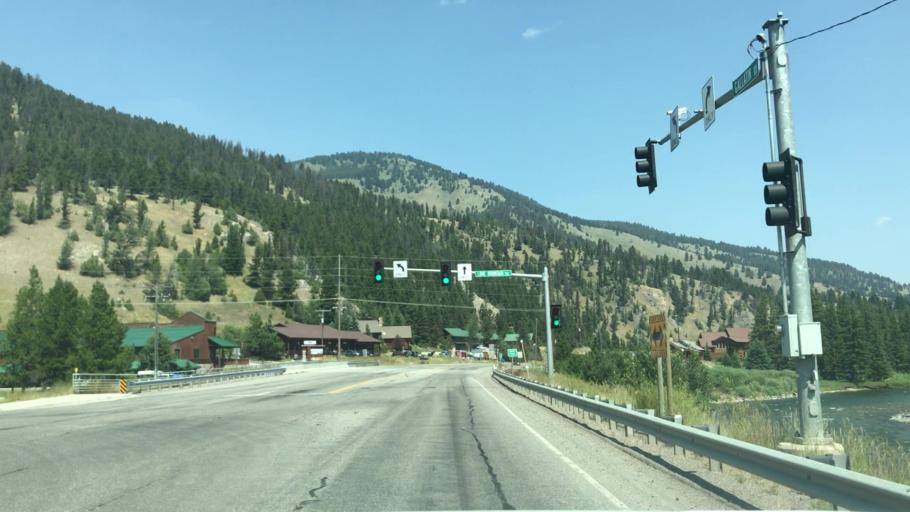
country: US
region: Montana
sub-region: Gallatin County
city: Big Sky
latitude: 45.2645
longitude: -111.2532
